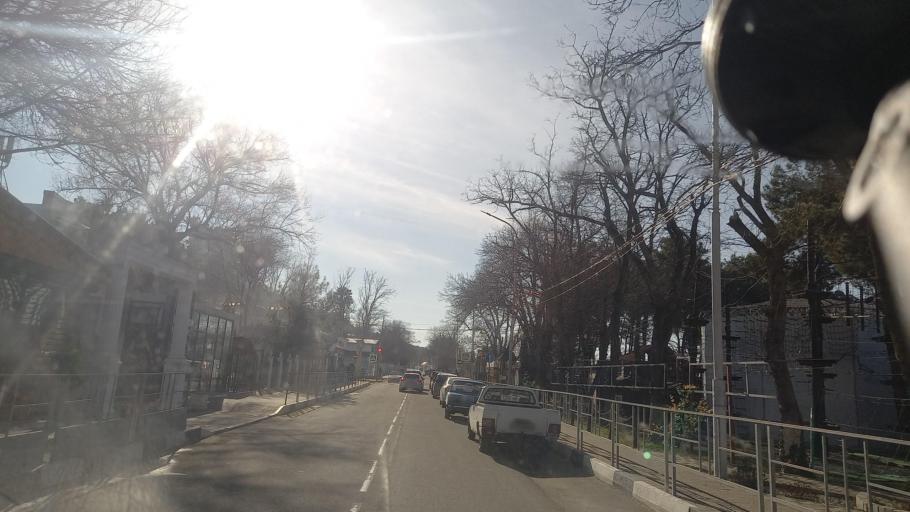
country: RU
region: Krasnodarskiy
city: Kabardinka
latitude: 44.6459
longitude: 37.9334
